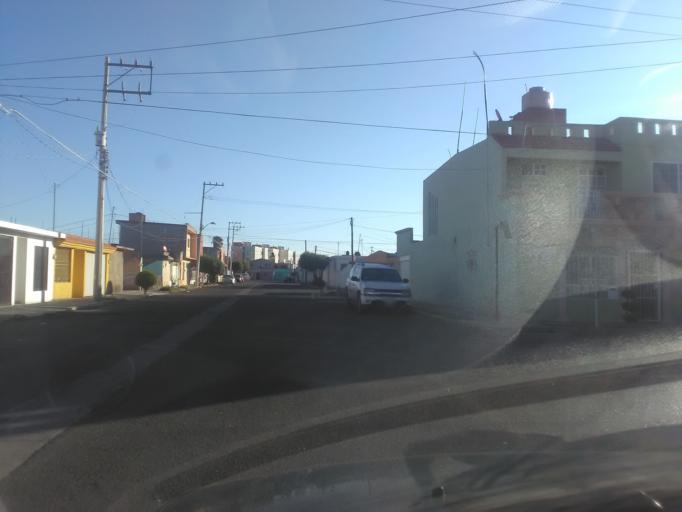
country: MX
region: Durango
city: Victoria de Durango
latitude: 23.9979
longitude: -104.7037
